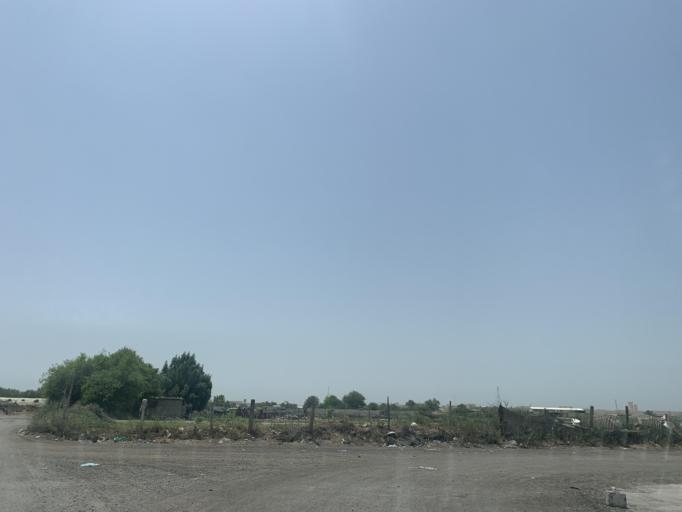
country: BH
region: Central Governorate
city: Madinat Hamad
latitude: 26.1536
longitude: 50.4944
